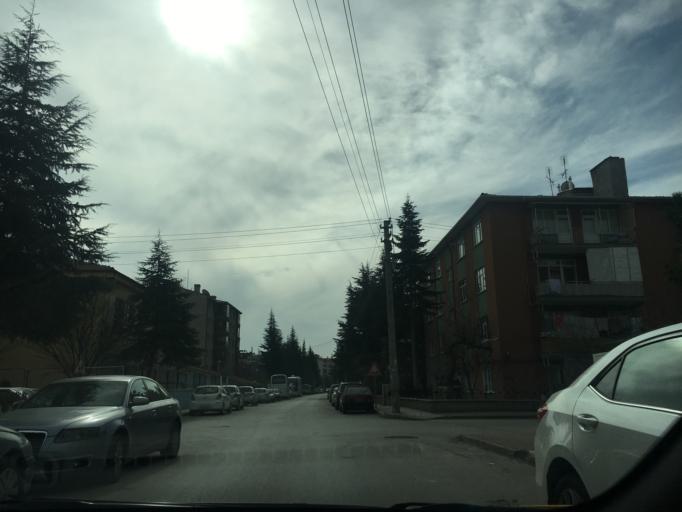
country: TR
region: Eskisehir
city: Eskisehir
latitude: 39.7722
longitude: 30.5046
